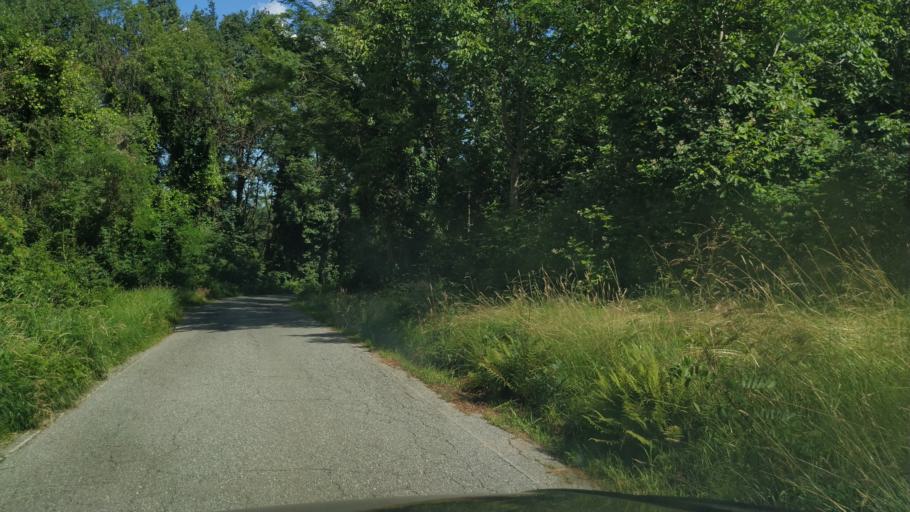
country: IT
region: Piedmont
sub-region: Provincia di Torino
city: Baldissero Canavese
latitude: 45.4127
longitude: 7.7164
